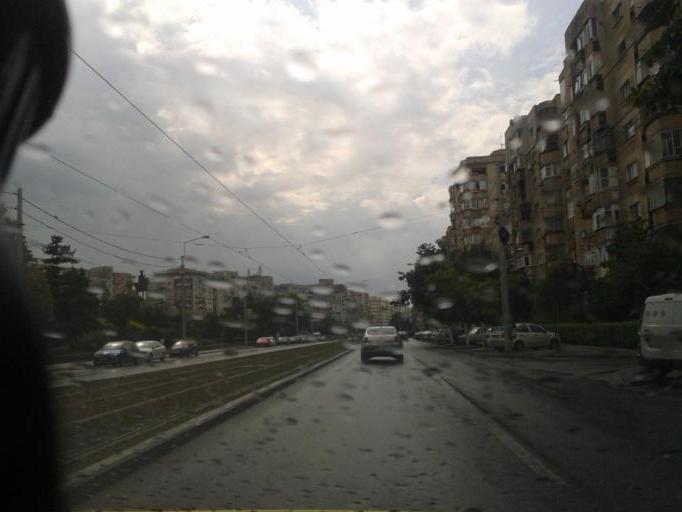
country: RO
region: Prahova
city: Ploiesti
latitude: 44.9472
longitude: 26.0138
